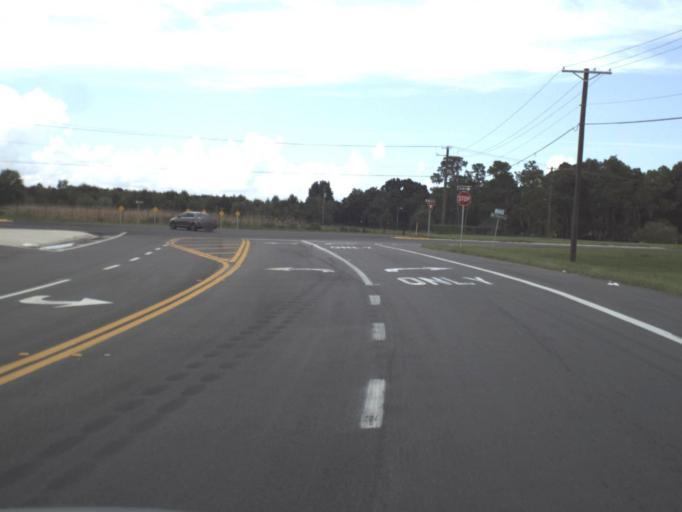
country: US
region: Florida
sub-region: Hillsborough County
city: Plant City
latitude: 28.0635
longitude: -82.1351
